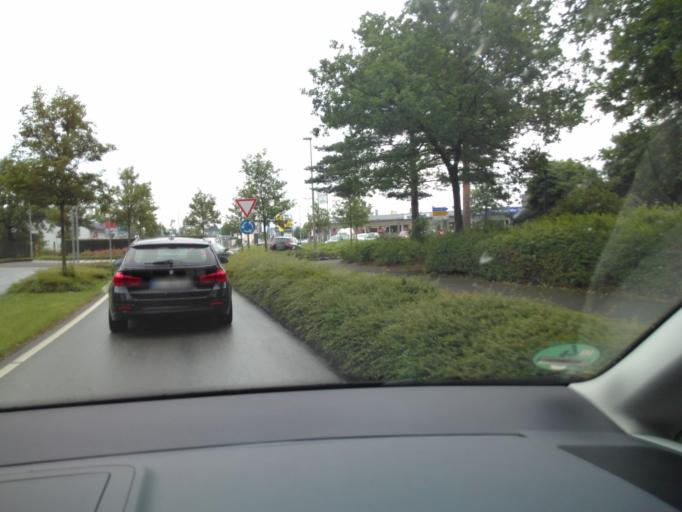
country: DE
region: North Rhine-Westphalia
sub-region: Regierungsbezirk Detmold
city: Oerlinghausen
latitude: 51.9024
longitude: 8.6356
